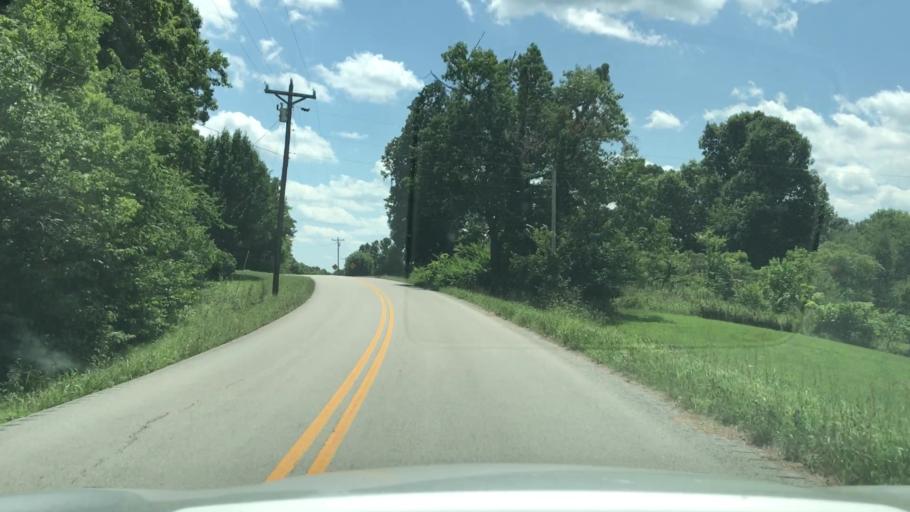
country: US
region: Kentucky
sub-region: Hopkins County
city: Nortonville
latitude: 37.0988
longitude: -87.3410
